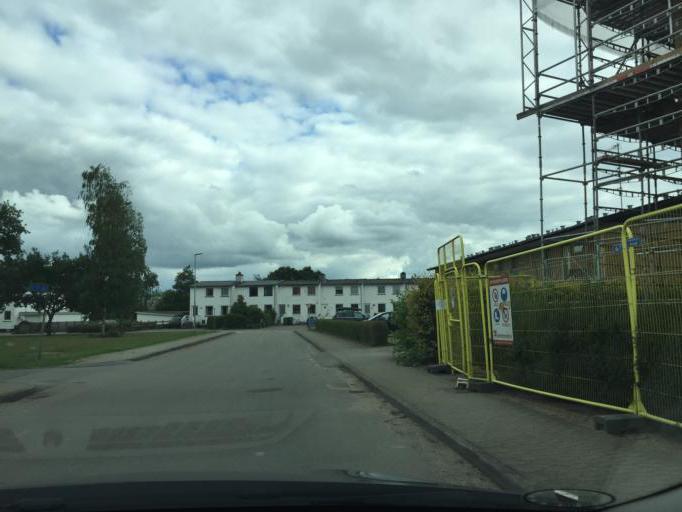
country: DK
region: South Denmark
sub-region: Haderslev Kommune
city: Vojens
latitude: 55.2443
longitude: 9.2967
